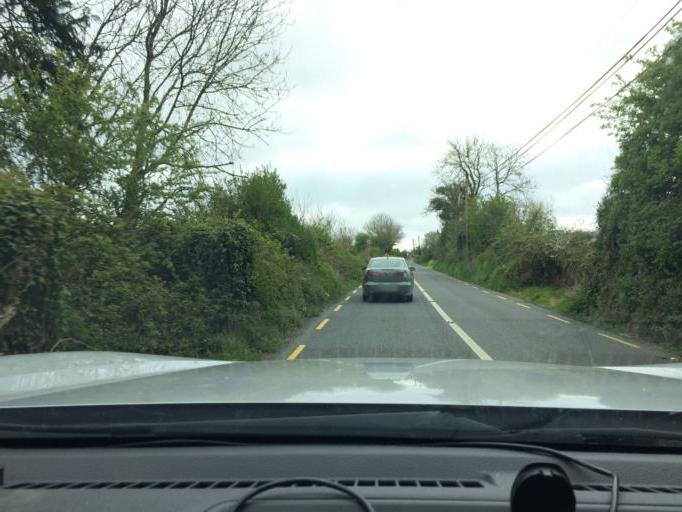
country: IE
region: Munster
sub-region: Waterford
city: Dungarvan
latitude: 52.0558
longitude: -7.6333
